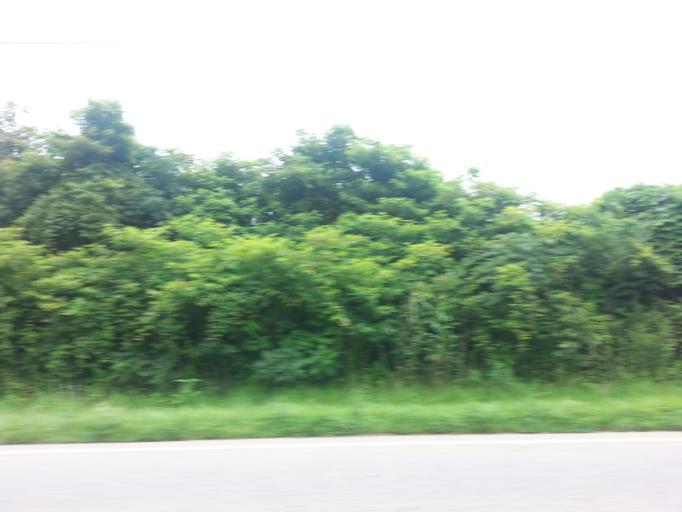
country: US
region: Ohio
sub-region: Brown County
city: Mount Orab
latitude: 39.0027
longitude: -83.9230
